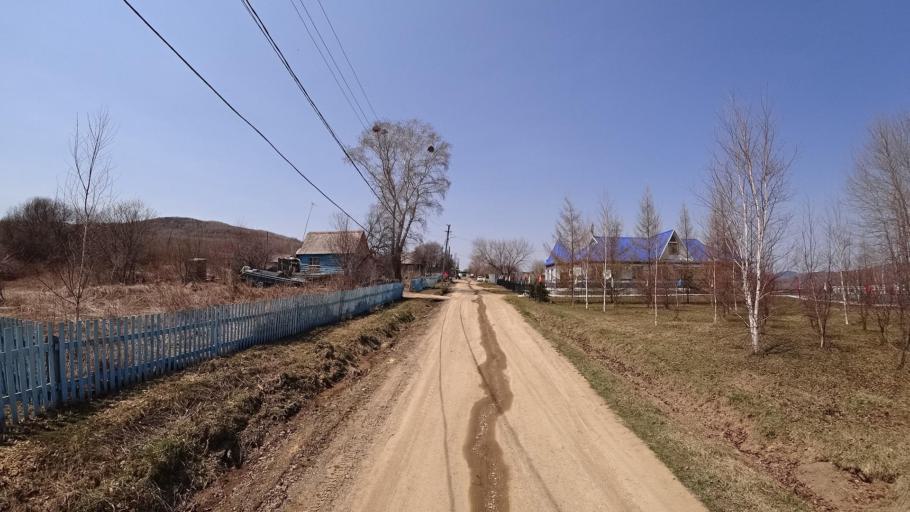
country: RU
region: Khabarovsk Krai
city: Selikhino
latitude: 50.6692
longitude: 137.3995
